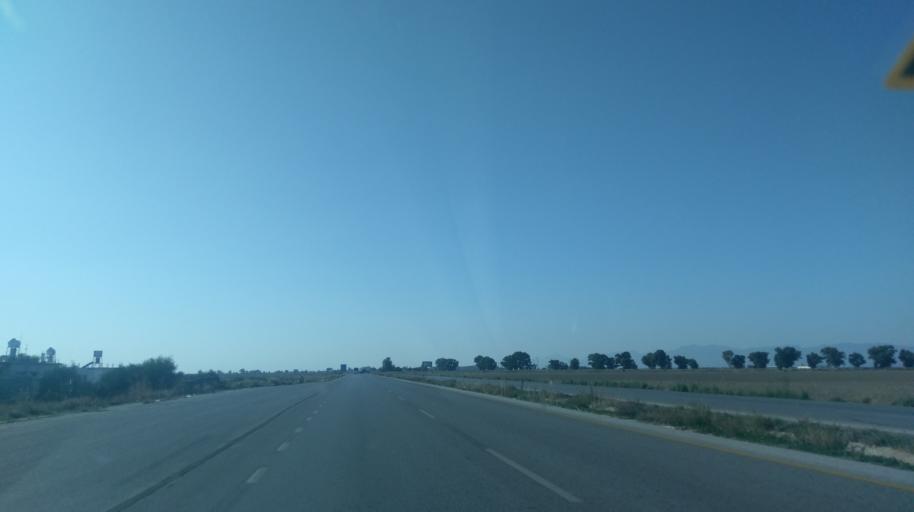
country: CY
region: Ammochostos
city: Lefkonoiko
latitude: 35.1712
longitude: 33.7821
